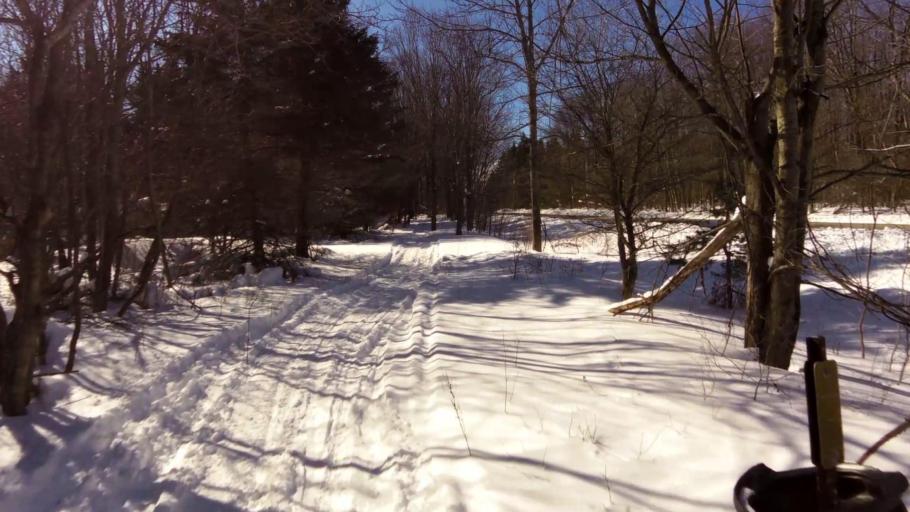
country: US
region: New York
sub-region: Allegany County
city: Cuba
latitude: 42.3305
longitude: -78.2833
